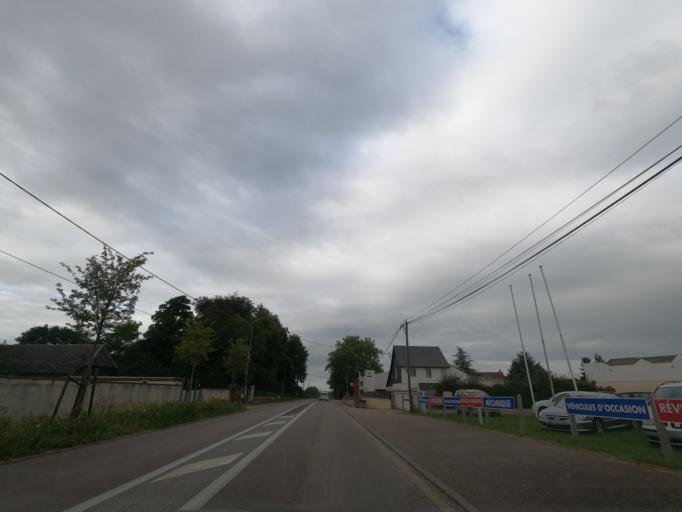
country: FR
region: Haute-Normandie
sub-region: Departement de l'Eure
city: Bourgtheroulde-Infreville
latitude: 49.2642
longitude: 0.8065
